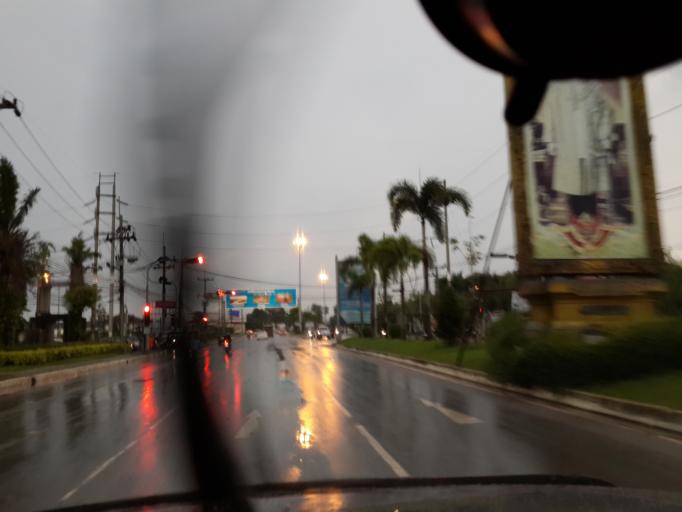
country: TH
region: Yala
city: Yala
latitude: 6.5527
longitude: 101.2700
